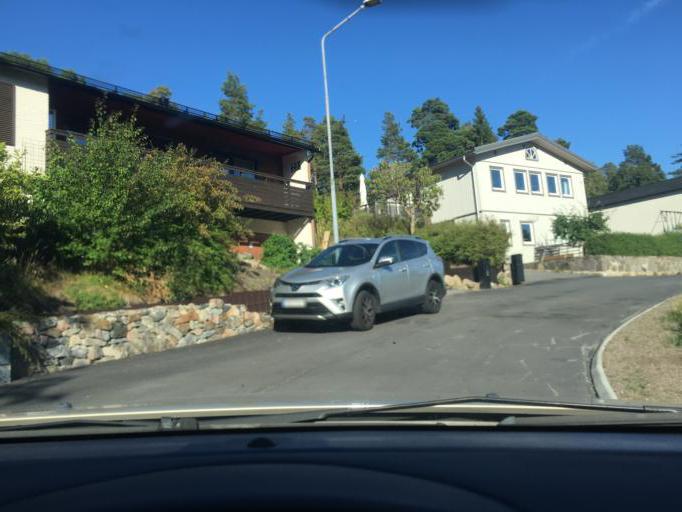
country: SE
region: Stockholm
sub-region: Nacka Kommun
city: Boo
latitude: 59.3263
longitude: 18.2429
